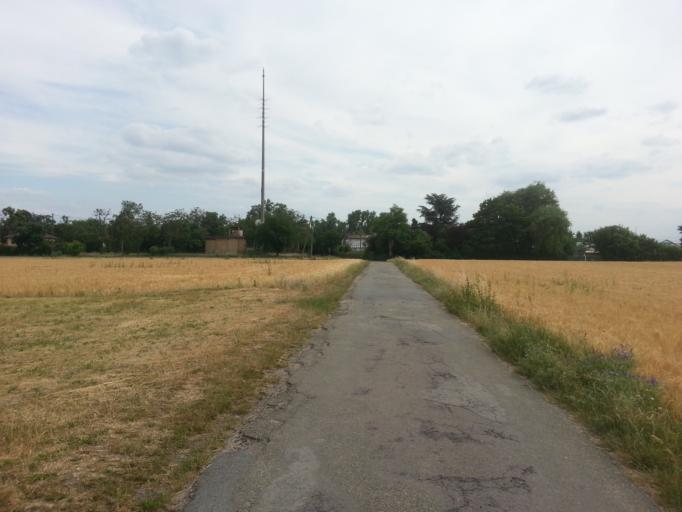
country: DE
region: Baden-Wuerttemberg
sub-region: Karlsruhe Region
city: Mannheim
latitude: 49.5262
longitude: 8.5209
